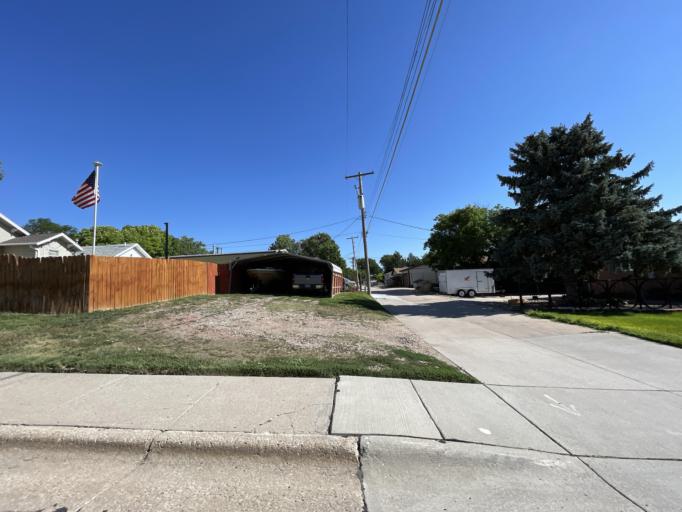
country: US
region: Nebraska
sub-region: Red Willow County
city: McCook
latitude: 40.2046
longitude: -100.6169
